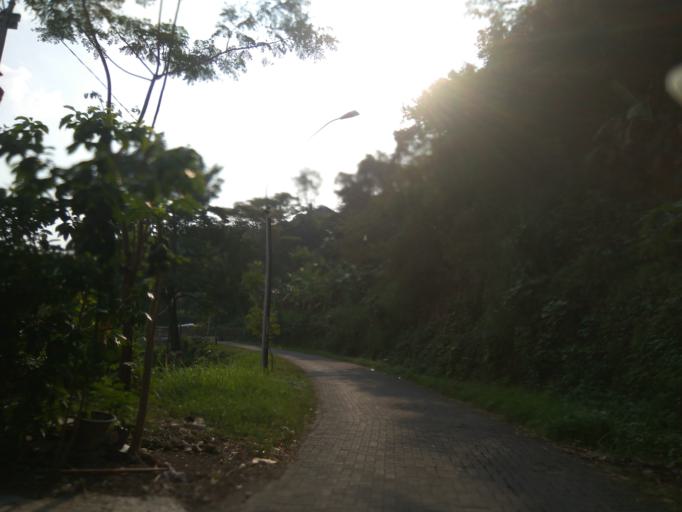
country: ID
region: Central Java
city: Semarang
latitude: -7.0172
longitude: 110.3836
